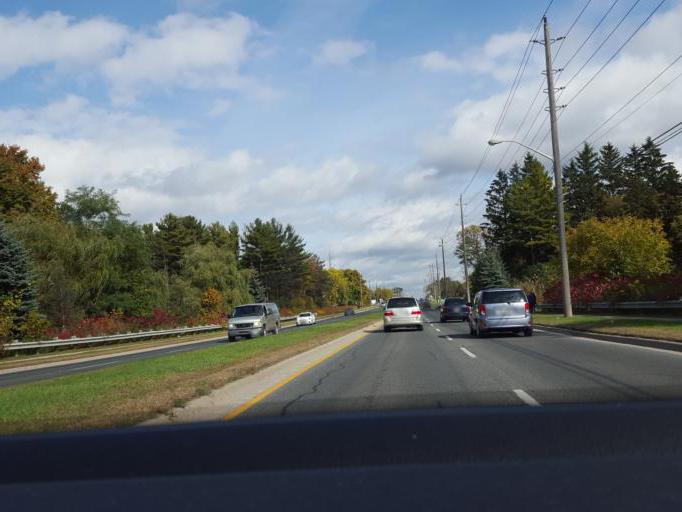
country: CA
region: Ontario
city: Oshawa
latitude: 43.9227
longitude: -78.9240
